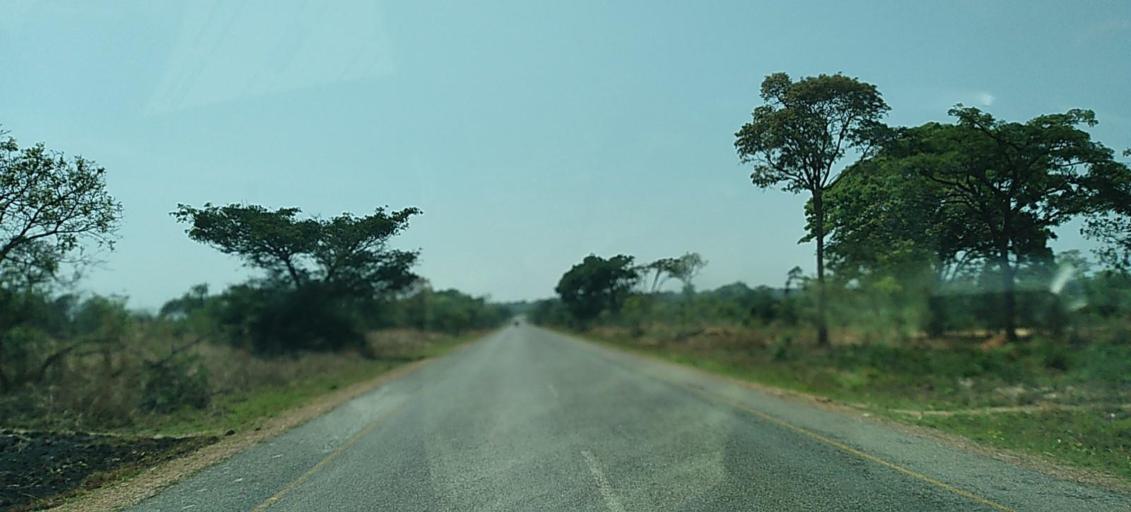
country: ZM
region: North-Western
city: Solwezi
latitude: -12.2836
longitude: 25.7776
